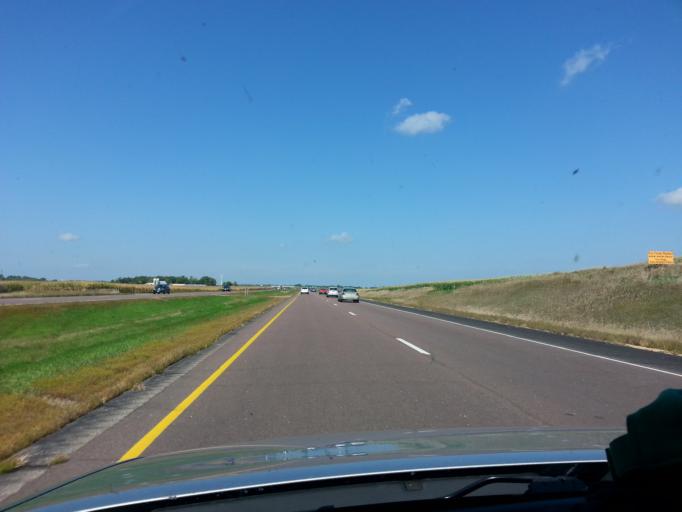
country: US
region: Minnesota
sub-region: Dakota County
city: Rosemount
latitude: 44.6946
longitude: -93.0236
